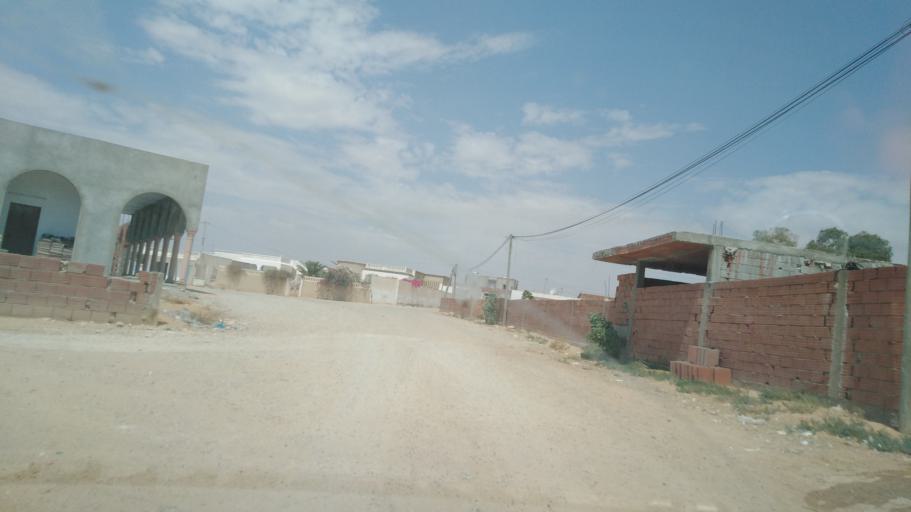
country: TN
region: Safaqis
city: Sfax
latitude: 34.7428
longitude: 10.5610
